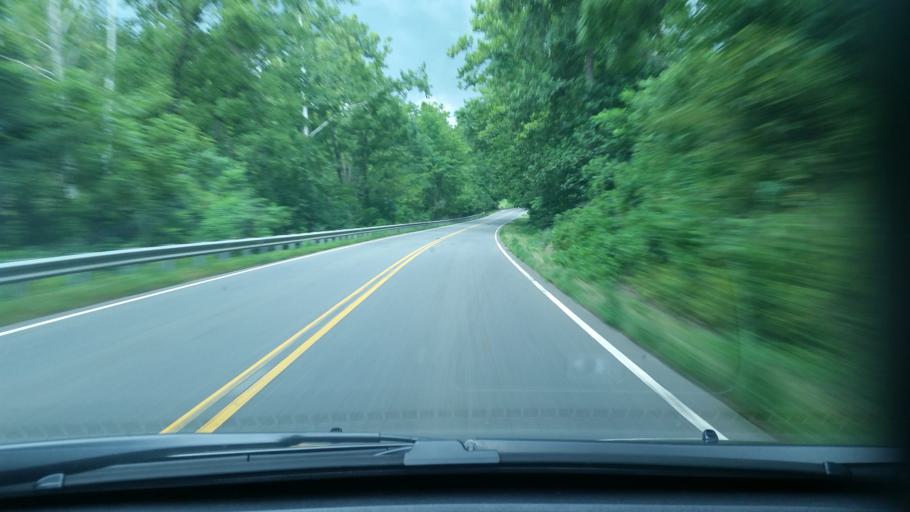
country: US
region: Virginia
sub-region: Nelson County
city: Nellysford
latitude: 37.8945
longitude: -78.8296
